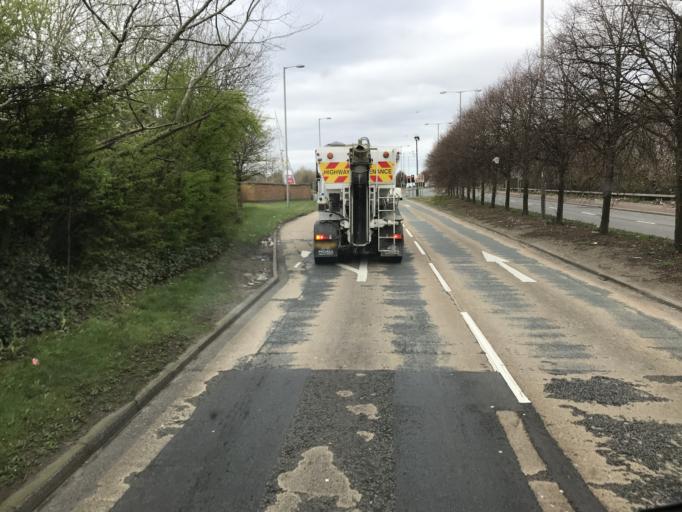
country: GB
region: England
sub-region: Borough of Halton
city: Hale
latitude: 53.3465
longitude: -2.8361
